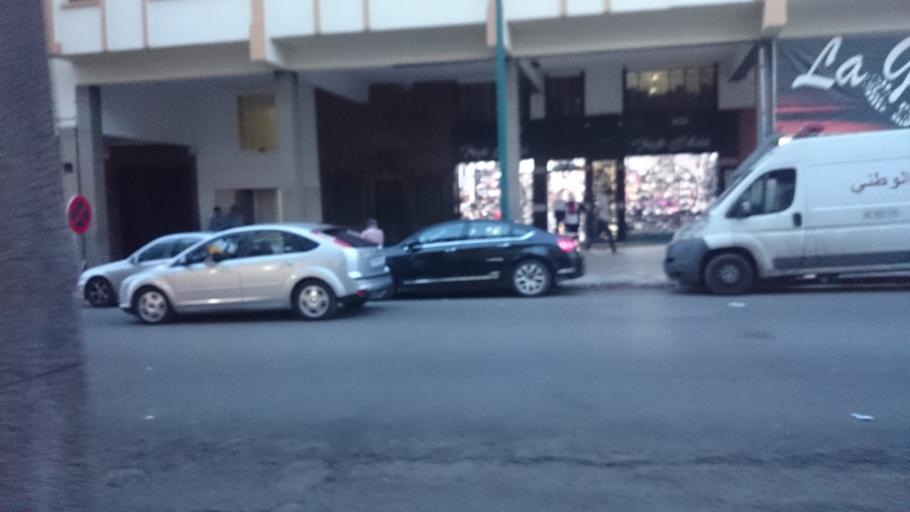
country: MA
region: Meknes-Tafilalet
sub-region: Meknes
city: Meknes
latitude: 33.8988
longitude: -5.5500
